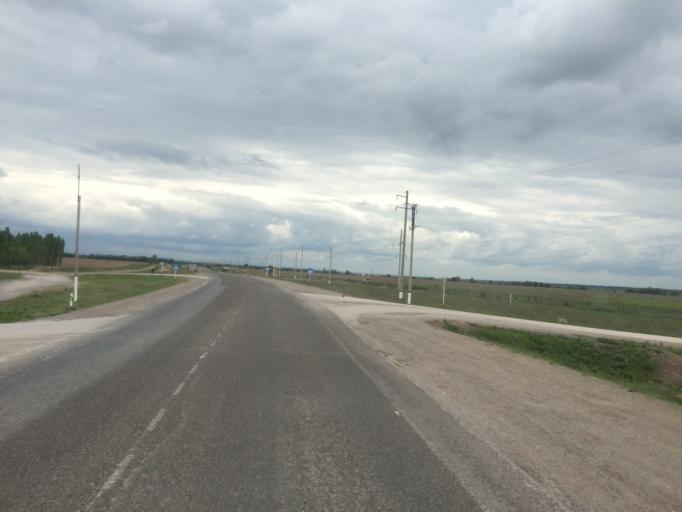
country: KG
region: Chuy
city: Sokuluk
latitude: 43.2465
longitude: 74.2998
